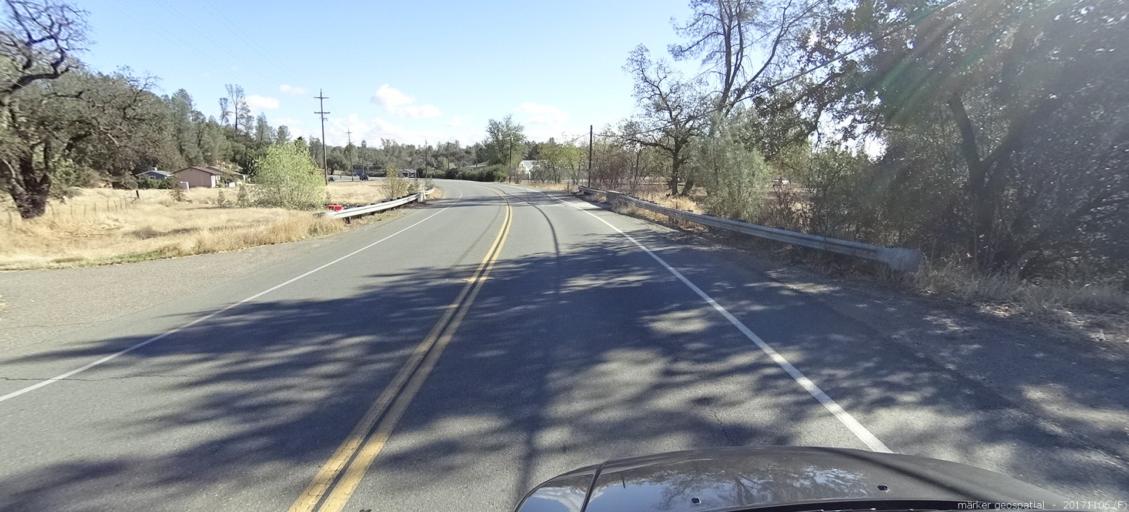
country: US
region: California
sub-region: Shasta County
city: Palo Cedro
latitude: 40.5886
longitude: -122.3024
